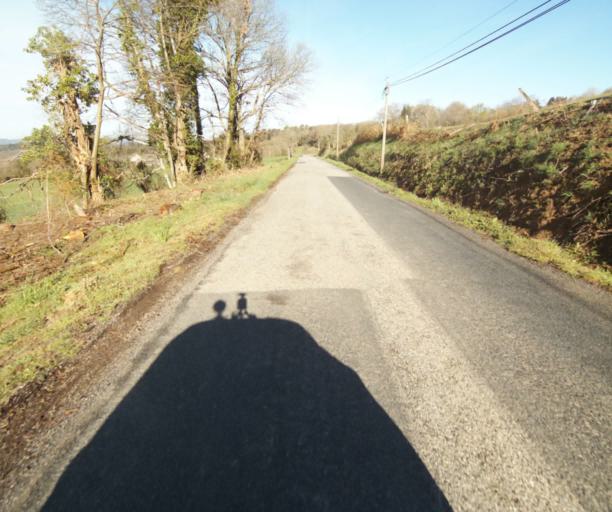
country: FR
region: Limousin
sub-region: Departement de la Correze
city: Laguenne
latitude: 45.2748
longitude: 1.8598
